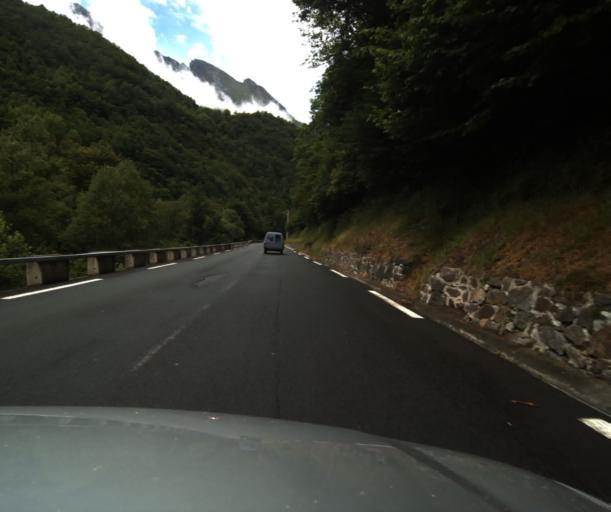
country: FR
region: Midi-Pyrenees
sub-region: Departement des Hautes-Pyrenees
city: Luz-Saint-Sauveur
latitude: 42.7994
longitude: 0.0150
